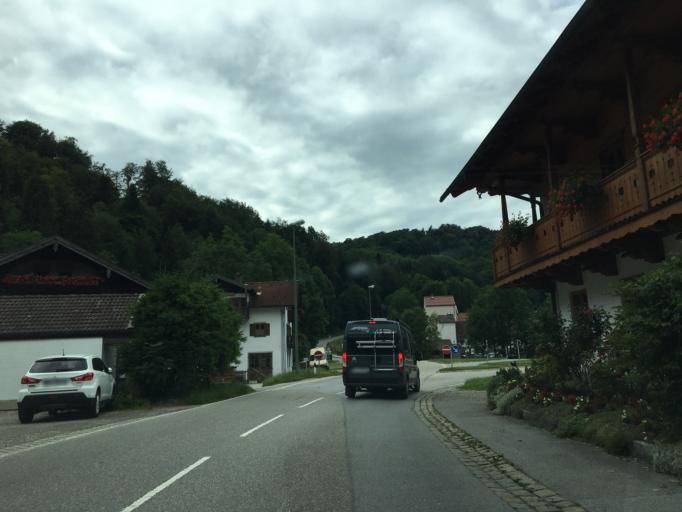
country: DE
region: Bavaria
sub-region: Upper Bavaria
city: Miesbach
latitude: 47.7801
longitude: 11.8760
